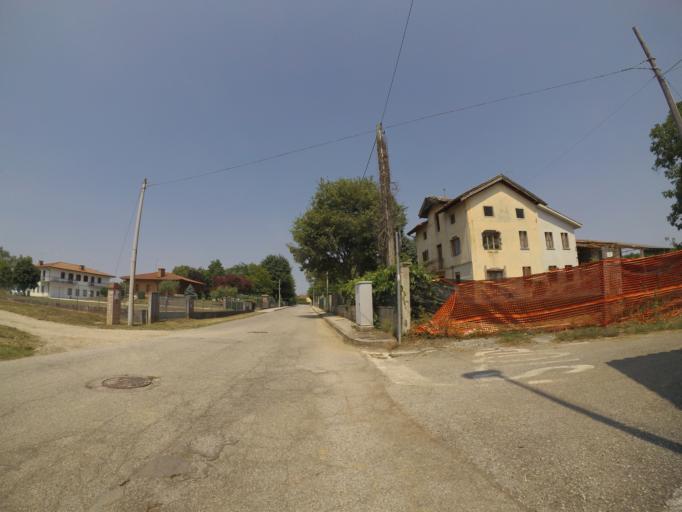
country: IT
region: Friuli Venezia Giulia
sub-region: Provincia di Udine
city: Basiliano-Vissandone
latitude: 46.0364
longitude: 13.1037
